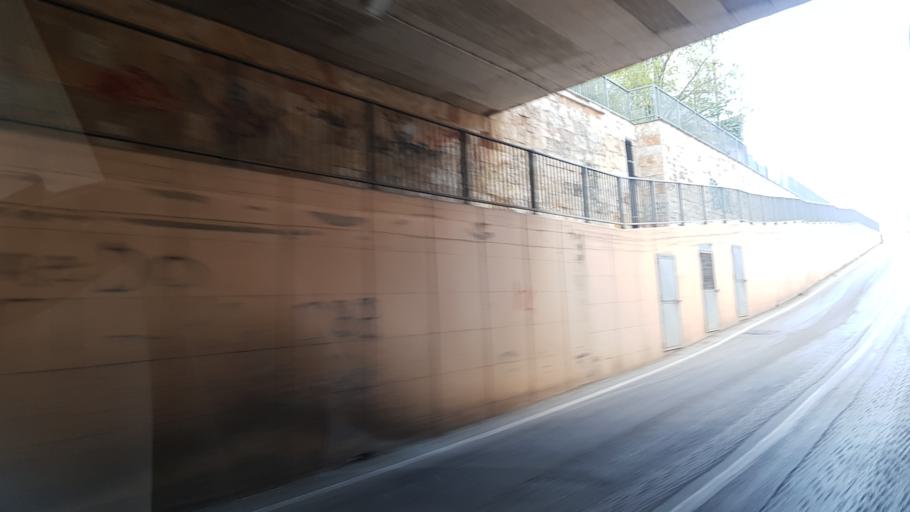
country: IT
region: Apulia
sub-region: Provincia di Brindisi
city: San Pietro Vernotico
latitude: 40.4907
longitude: 17.9998
